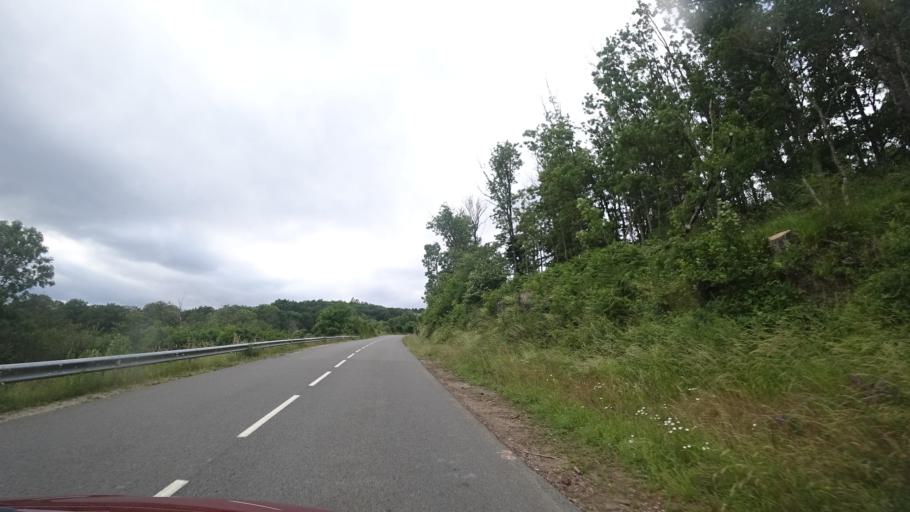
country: FR
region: Midi-Pyrenees
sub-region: Departement de l'Aveyron
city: Saint-Georges-de-Luzencon
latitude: 44.1198
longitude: 2.8952
